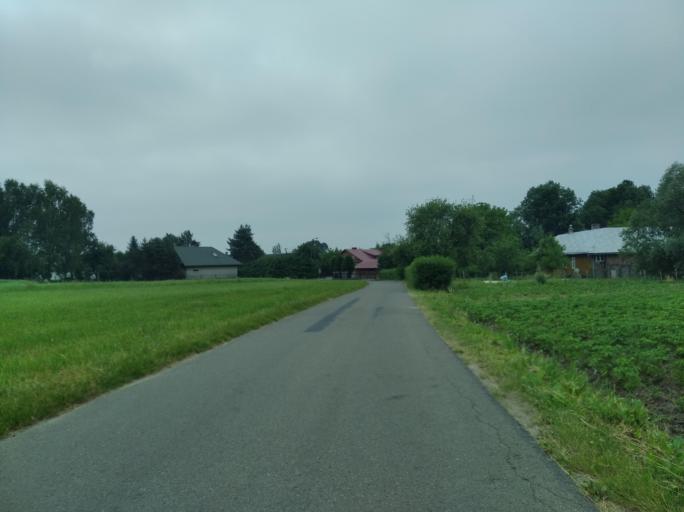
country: PL
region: Subcarpathian Voivodeship
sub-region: Powiat brzozowski
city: Jablonica Polska
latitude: 49.6847
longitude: 21.8891
